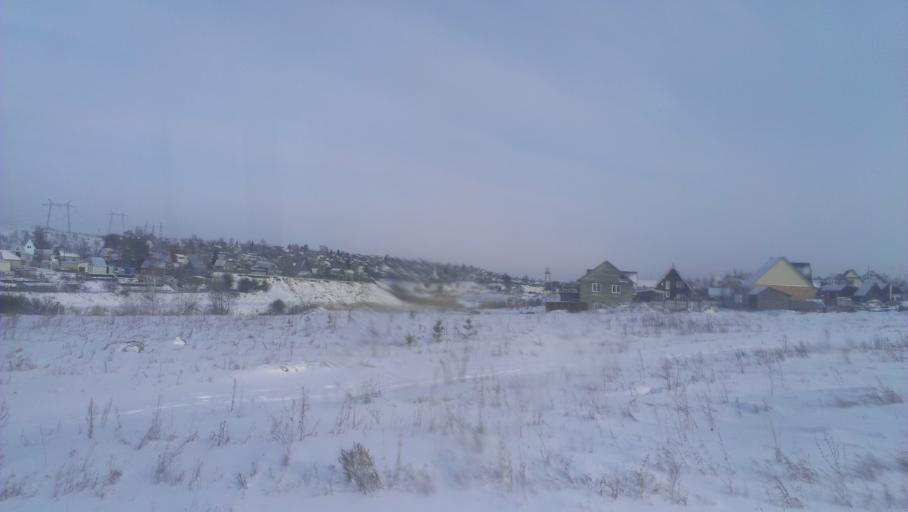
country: RU
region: Altai Krai
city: Gon'ba
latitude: 53.4142
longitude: 83.5512
